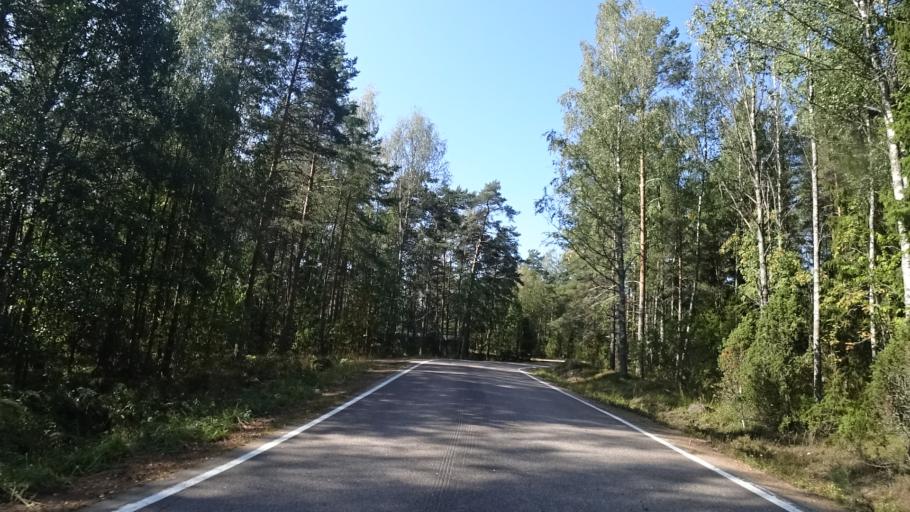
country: FI
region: Kymenlaakso
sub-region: Kotka-Hamina
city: Hamina
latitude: 60.5153
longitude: 27.3635
